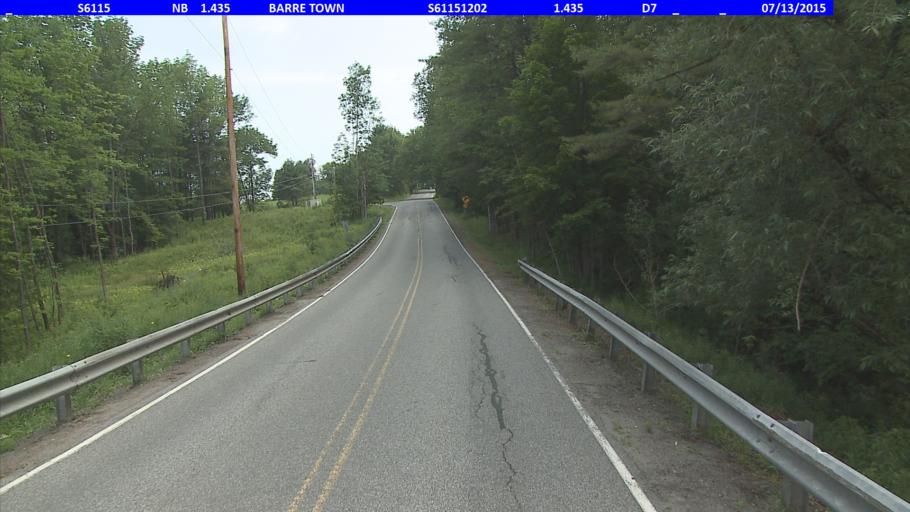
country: US
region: Vermont
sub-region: Washington County
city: Barre
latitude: 44.2182
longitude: -72.4733
